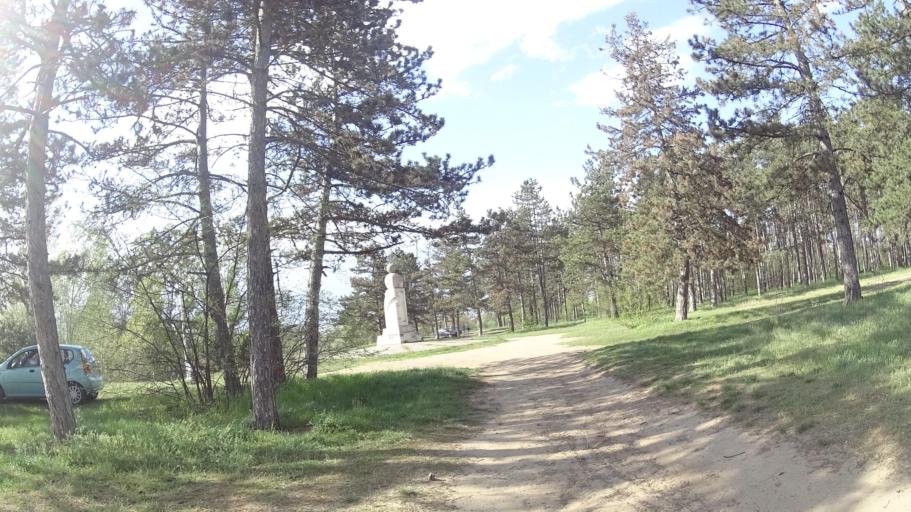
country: HU
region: Pest
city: Veresegyhaz
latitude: 47.6412
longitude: 19.2778
